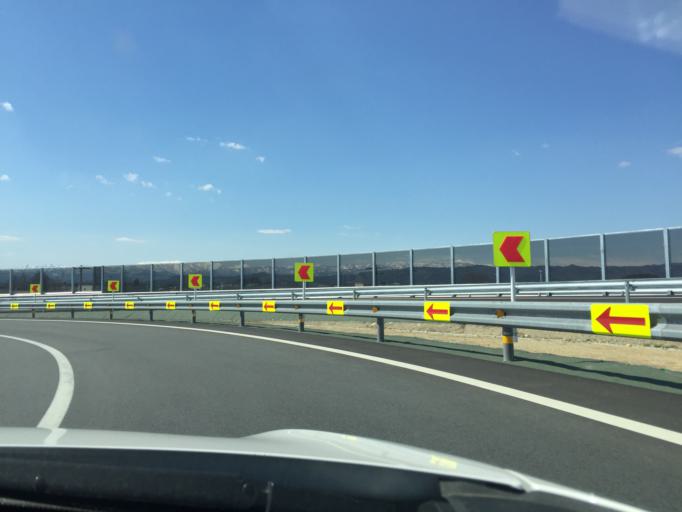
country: JP
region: Yamagata
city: Takahata
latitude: 38.0261
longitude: 140.1643
